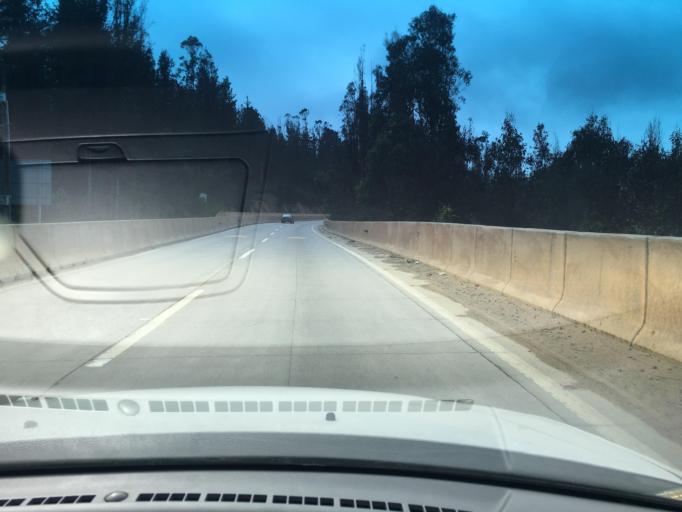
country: CL
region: Valparaiso
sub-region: Provincia de Valparaiso
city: Vina del Mar
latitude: -33.1026
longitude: -71.5727
